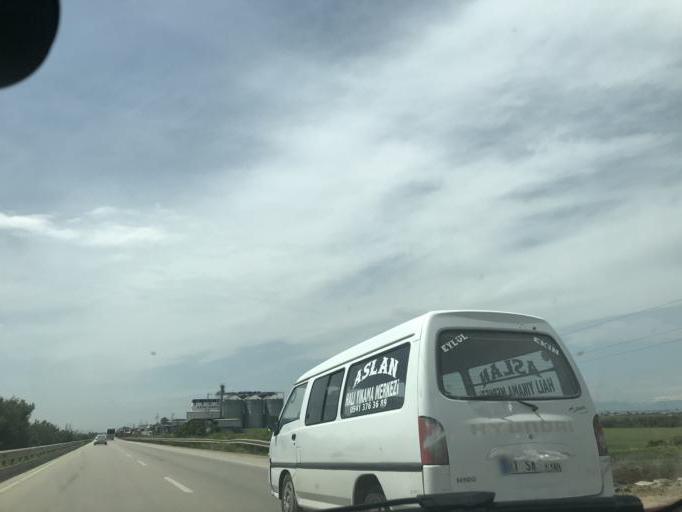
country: TR
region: Adana
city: Yuregir
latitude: 36.9775
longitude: 35.4721
